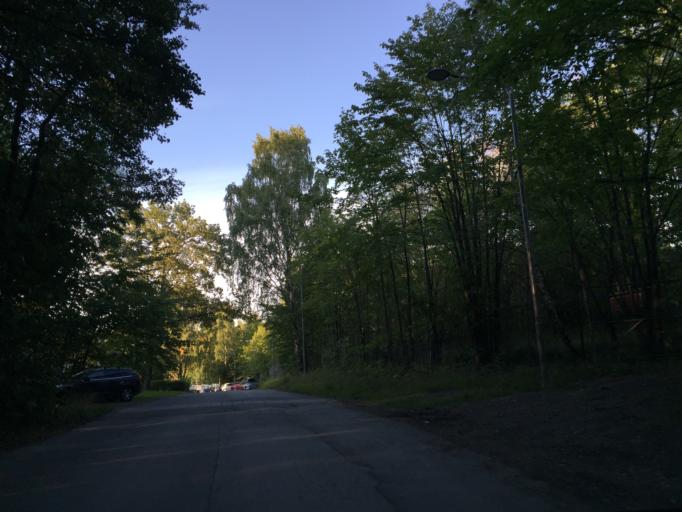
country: NO
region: Akershus
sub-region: Baerum
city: Lysaker
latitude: 59.9017
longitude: 10.6138
